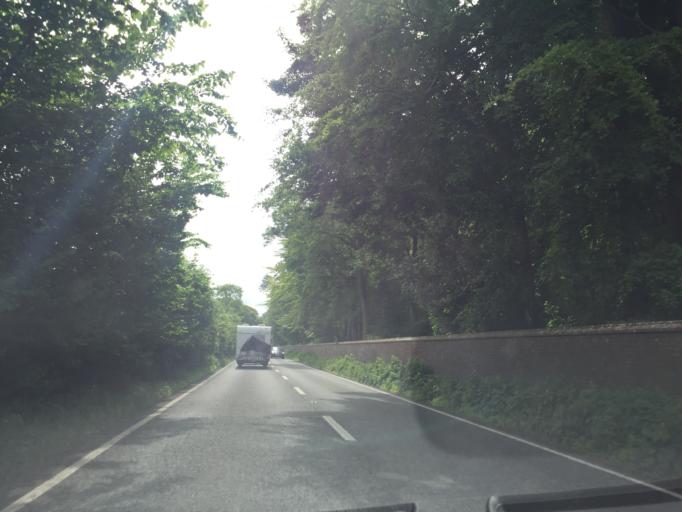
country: GB
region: England
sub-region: Dorset
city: Lytchett Matravers
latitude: 50.7927
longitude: -2.1029
